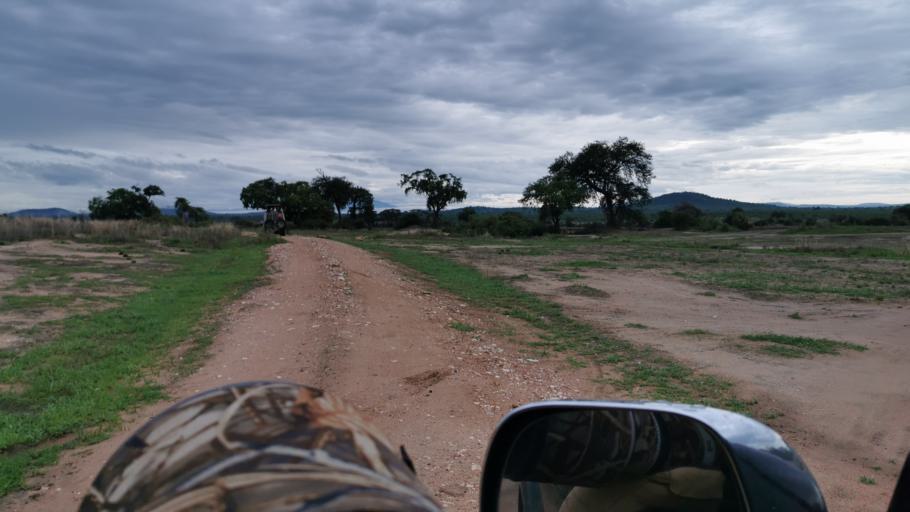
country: TZ
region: Iringa
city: Mafinga
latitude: -7.6638
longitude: 34.9600
